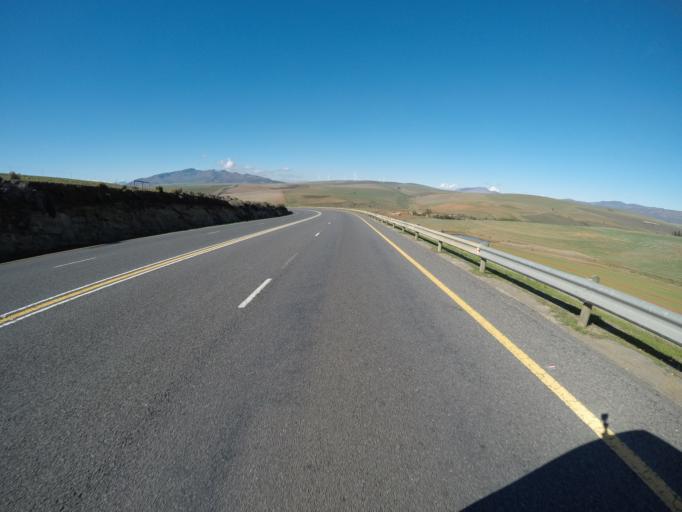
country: ZA
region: Western Cape
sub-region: Overberg District Municipality
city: Caledon
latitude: -34.2120
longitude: 19.3269
